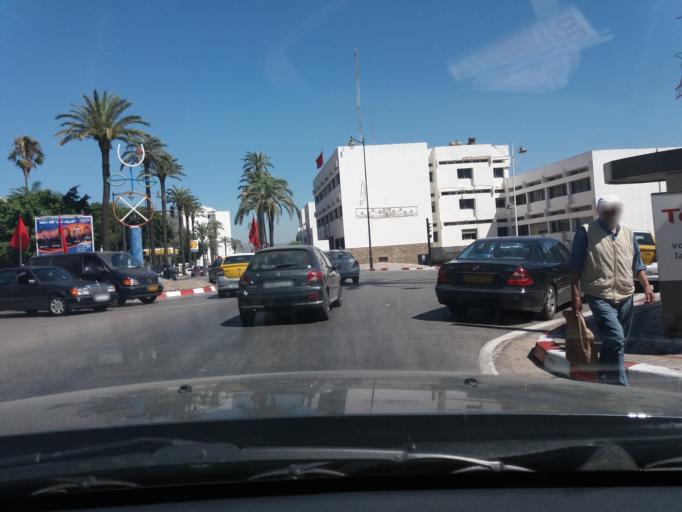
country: MA
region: Tanger-Tetouan
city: Tetouan
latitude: 35.5686
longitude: -5.3802
